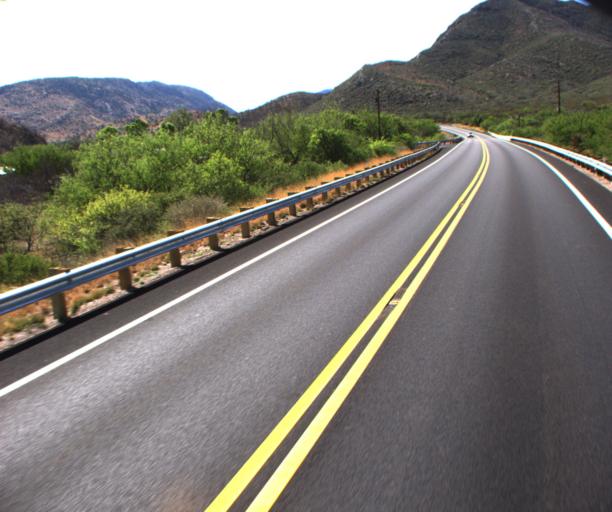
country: US
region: Arizona
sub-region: Cochise County
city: Bisbee
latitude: 31.5121
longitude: -110.0176
